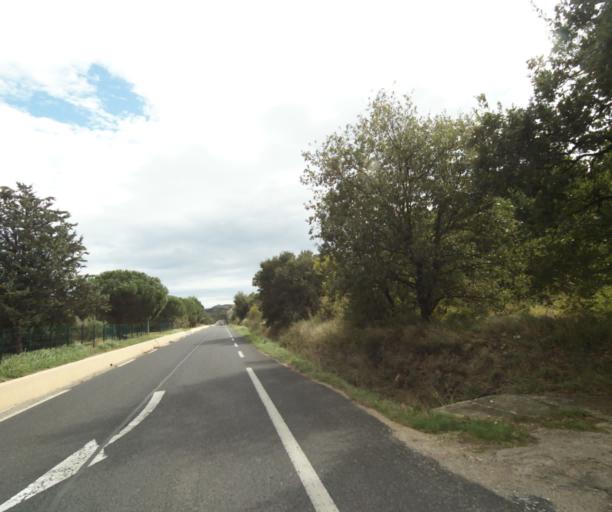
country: FR
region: Languedoc-Roussillon
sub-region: Departement des Pyrenees-Orientales
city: Argelers
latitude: 42.5390
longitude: 3.0391
